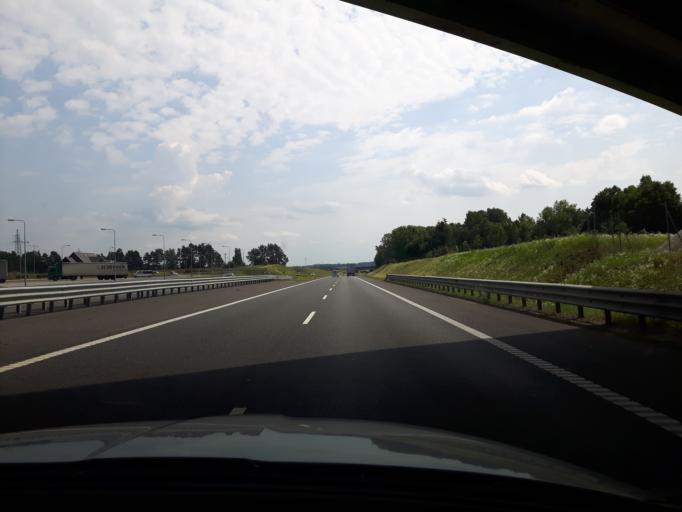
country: PL
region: Warmian-Masurian Voivodeship
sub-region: Powiat olsztynski
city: Olsztynek
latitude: 53.5154
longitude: 20.2959
